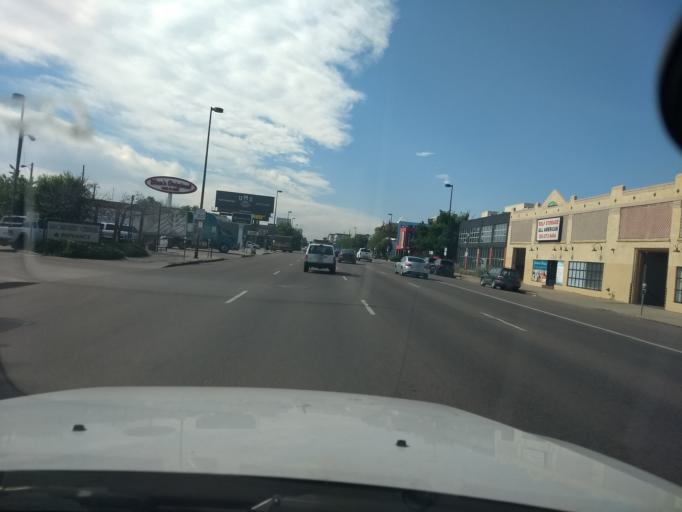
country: US
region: Colorado
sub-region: Denver County
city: Denver
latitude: 39.7251
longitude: -104.9875
